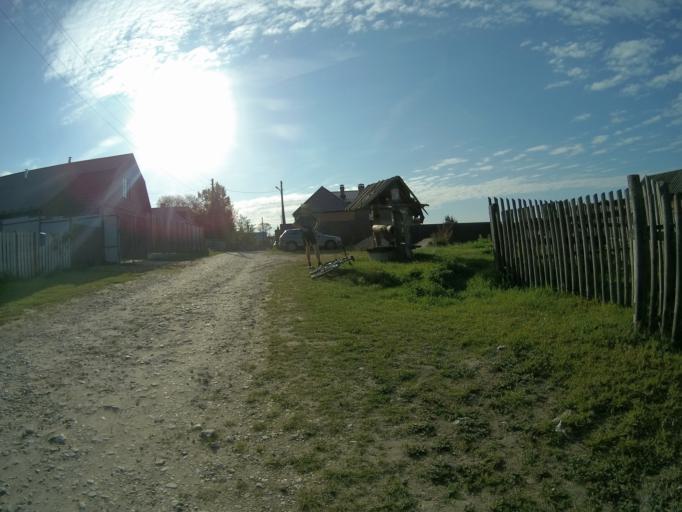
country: RU
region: Vladimir
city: Sobinka
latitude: 55.9112
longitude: 40.0377
